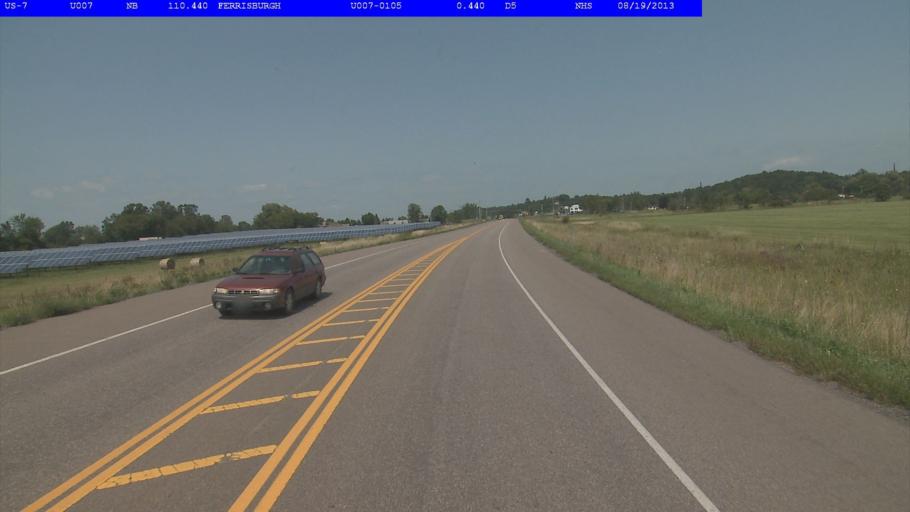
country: US
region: Vermont
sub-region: Addison County
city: Vergennes
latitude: 44.1681
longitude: -73.2394
